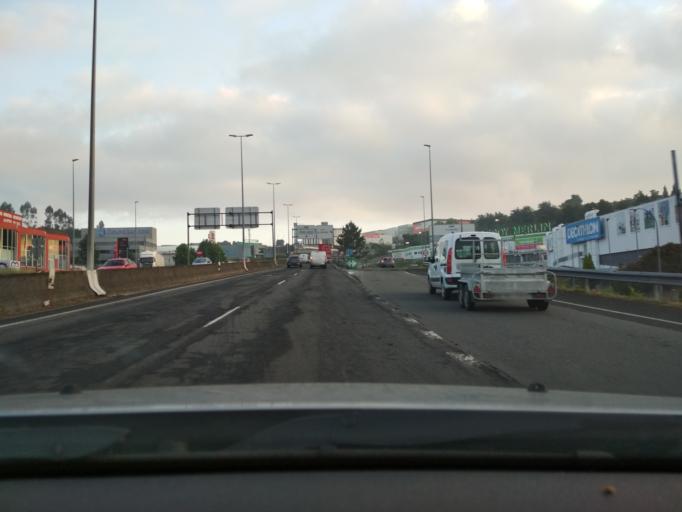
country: ES
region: Galicia
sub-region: Provincia da Coruna
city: Santiago de Compostela
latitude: 42.9008
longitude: -8.5108
